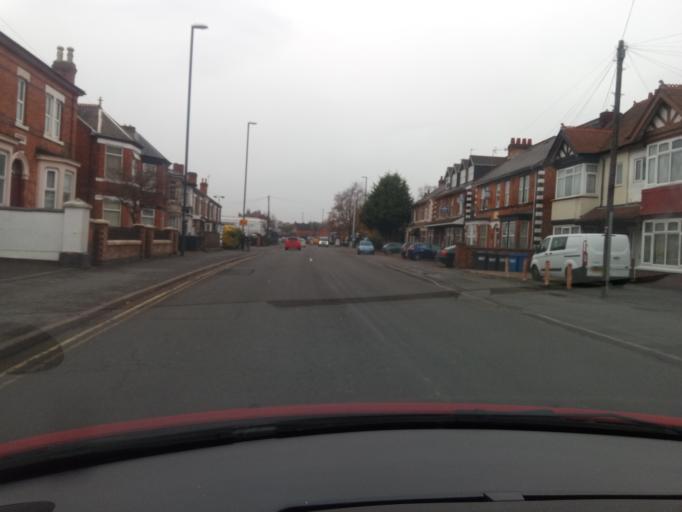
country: GB
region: England
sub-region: Derby
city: Derby
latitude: 52.9012
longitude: -1.4372
